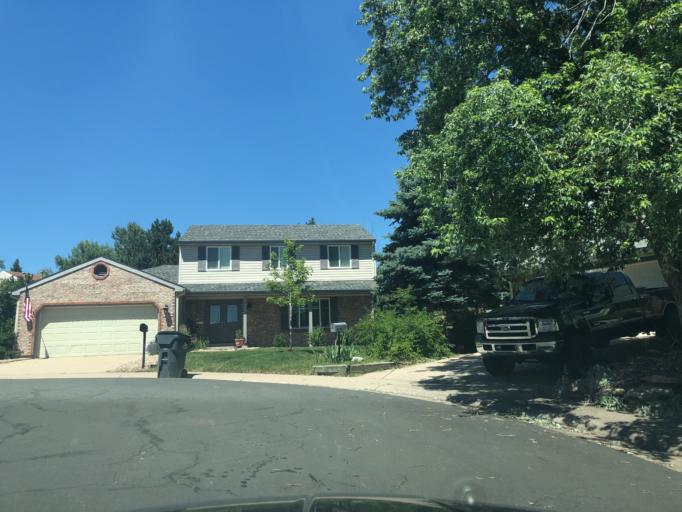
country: US
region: Colorado
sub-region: Arapahoe County
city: Dove Valley
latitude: 39.6181
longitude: -104.7858
